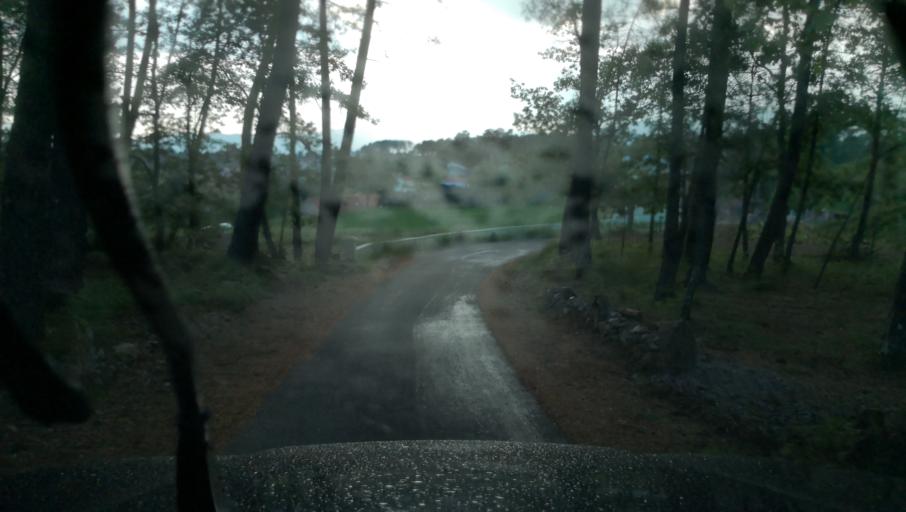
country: PT
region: Vila Real
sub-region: Vila Real
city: Vila Real
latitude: 41.3156
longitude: -7.6773
